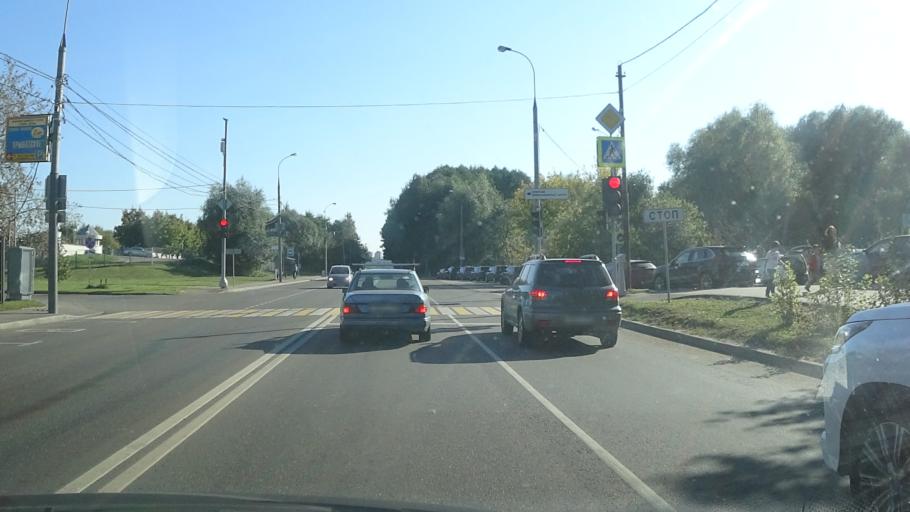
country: RU
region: Moscow
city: Shchukino
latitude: 55.7677
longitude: 37.4287
